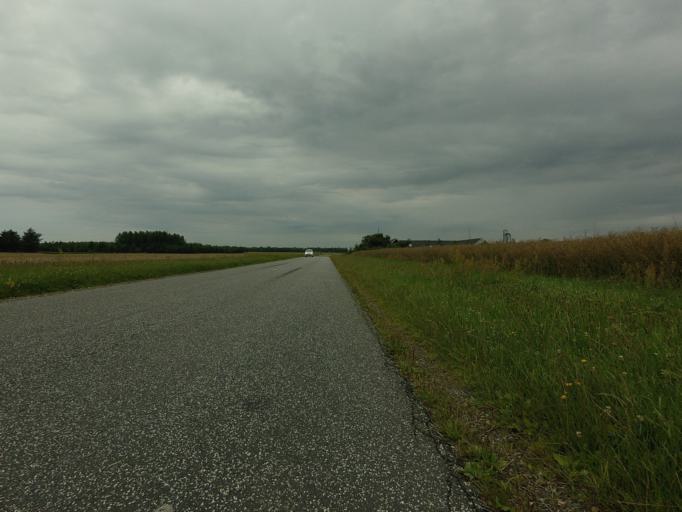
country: DK
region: North Denmark
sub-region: Alborg Kommune
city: Vadum
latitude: 57.1284
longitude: 9.8543
